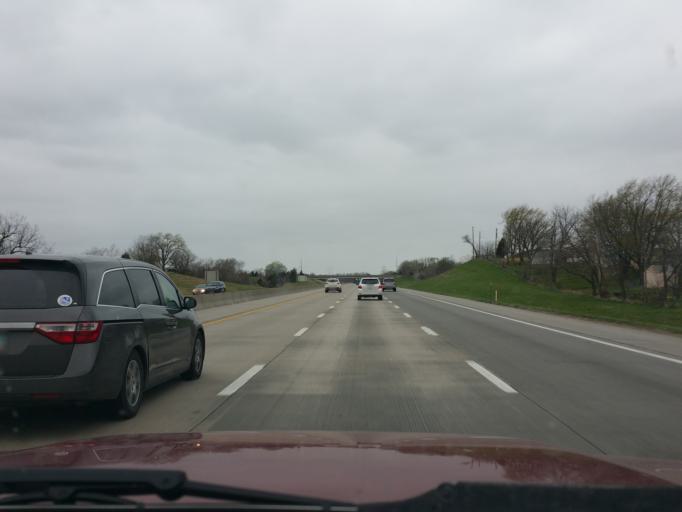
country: US
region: Kansas
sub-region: Wyandotte County
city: Edwardsville
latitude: 39.1051
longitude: -94.7718
